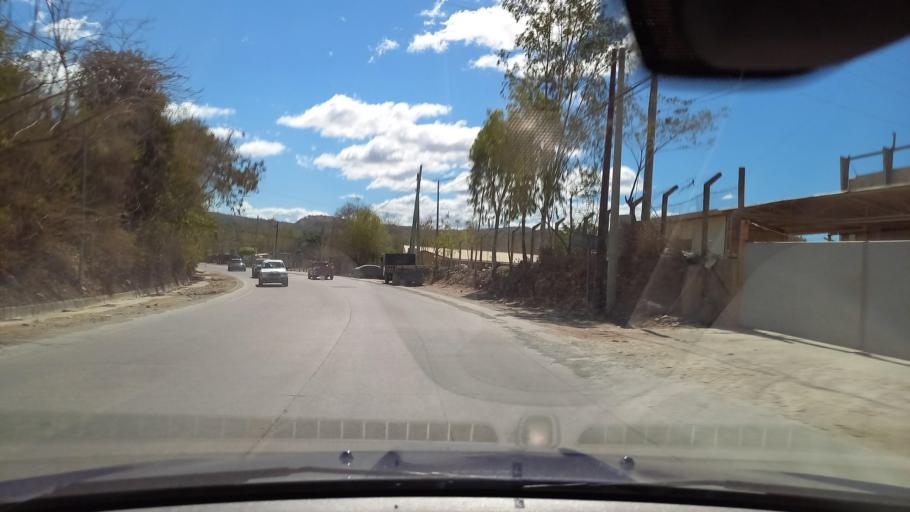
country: SV
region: Santa Ana
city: Metapan
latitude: 14.3433
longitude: -89.4538
